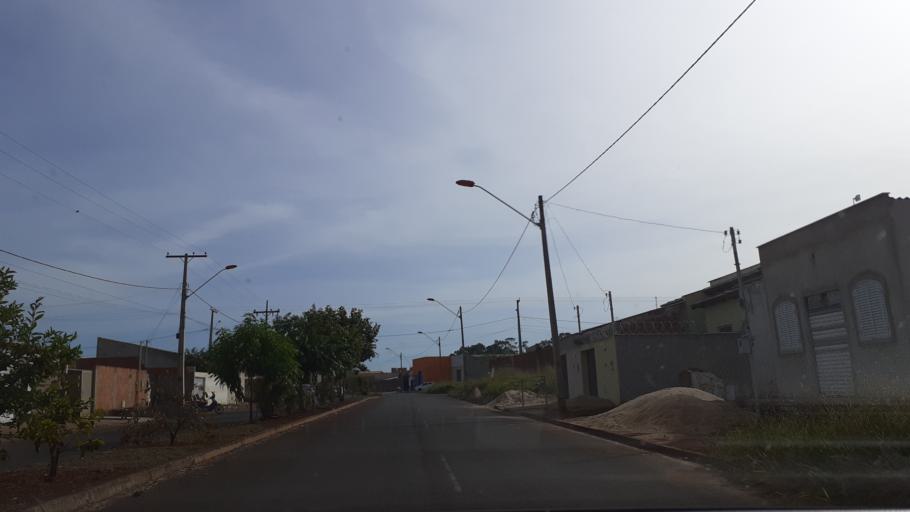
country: BR
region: Goias
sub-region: Itumbiara
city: Itumbiara
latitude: -18.4180
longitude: -49.2519
